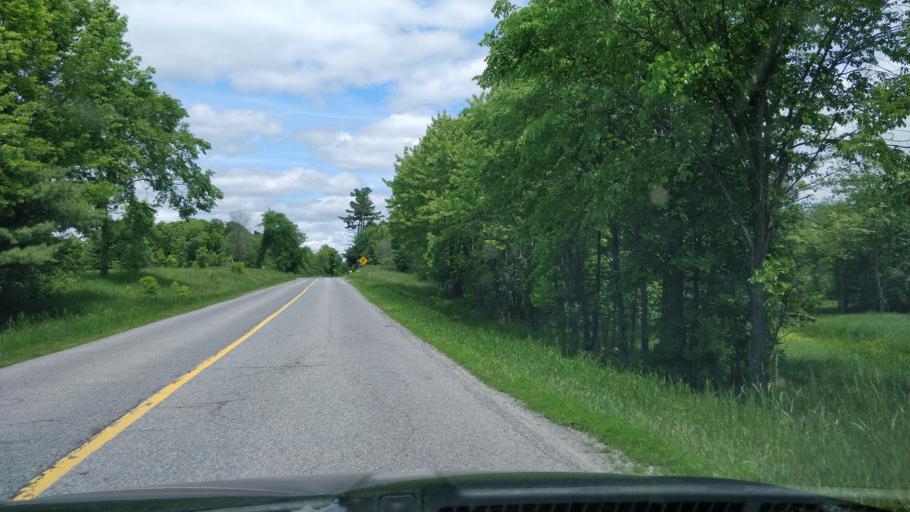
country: CA
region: Ontario
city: Perth
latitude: 44.7523
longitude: -76.4849
